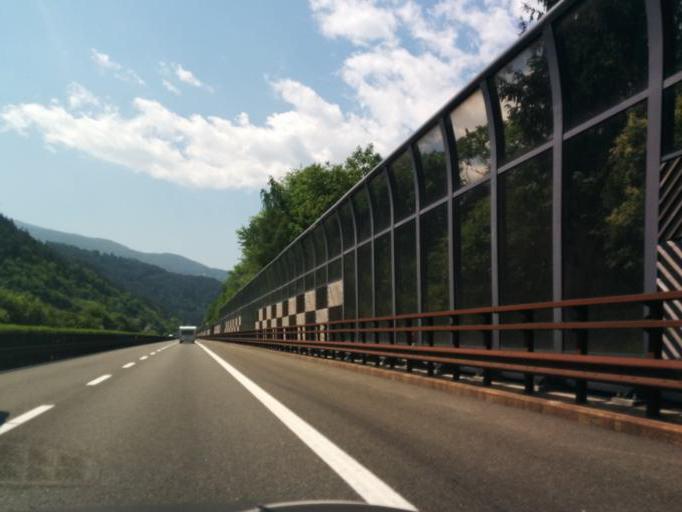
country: IT
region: Trentino-Alto Adige
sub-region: Bolzano
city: Velturno
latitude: 46.6685
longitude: 11.6154
